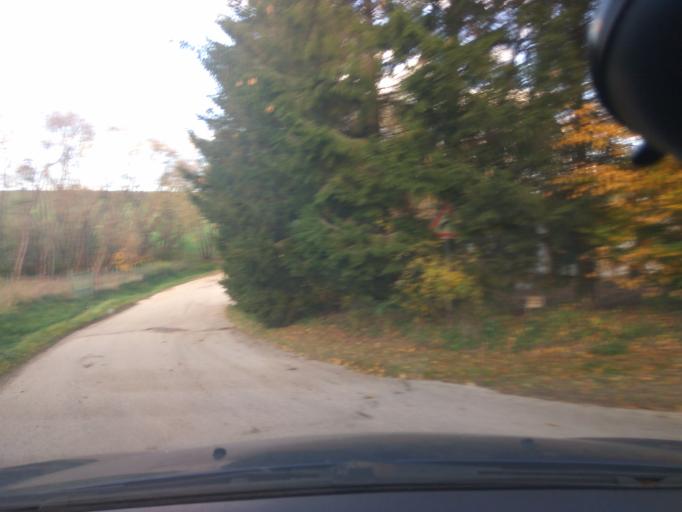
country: SK
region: Trnavsky
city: Vrbove
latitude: 48.6371
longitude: 17.6331
